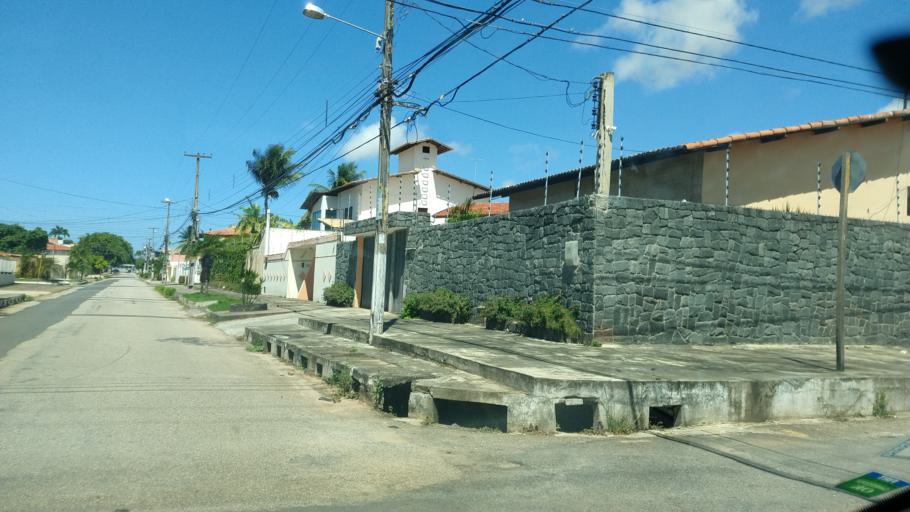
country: BR
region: Rio Grande do Norte
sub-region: Natal
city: Natal
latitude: -5.8454
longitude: -35.2021
